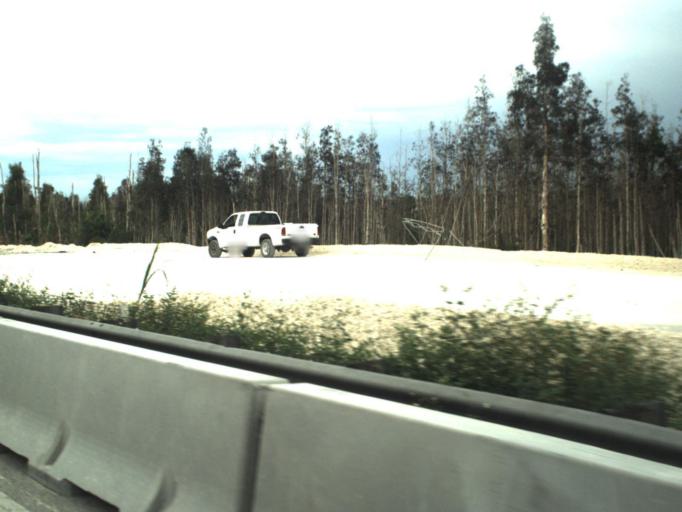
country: US
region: Florida
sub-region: Miami-Dade County
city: Kendall West
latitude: 25.7446
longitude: -80.4807
